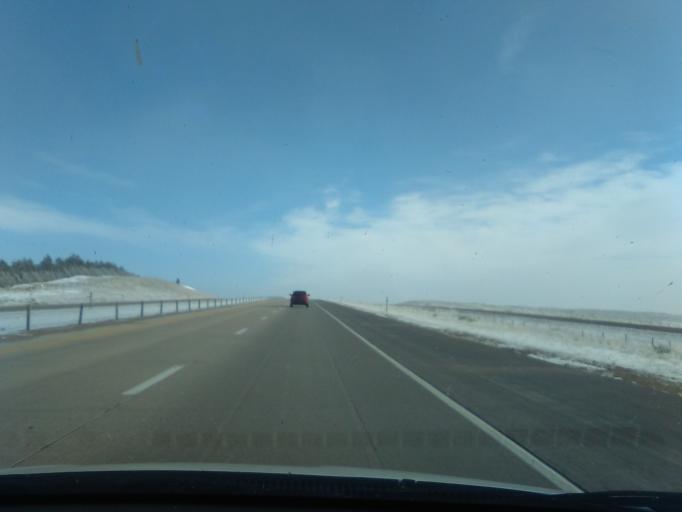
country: US
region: Wyoming
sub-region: Laramie County
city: Pine Bluffs
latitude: 41.1587
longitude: -104.3148
